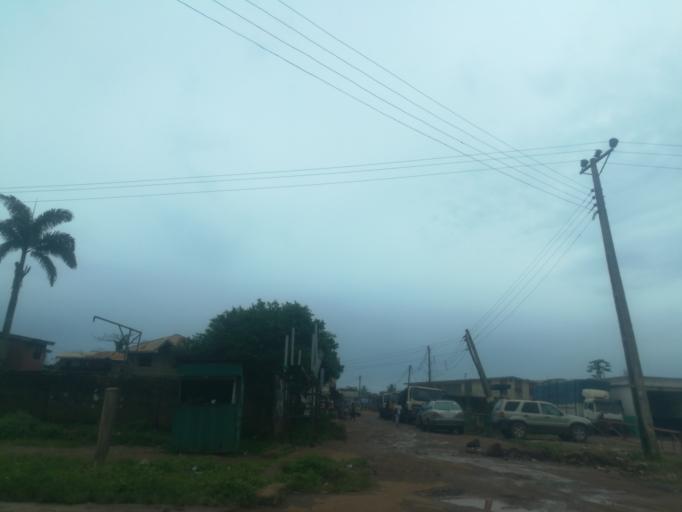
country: NG
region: Oyo
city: Ibadan
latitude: 7.3917
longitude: 3.9668
